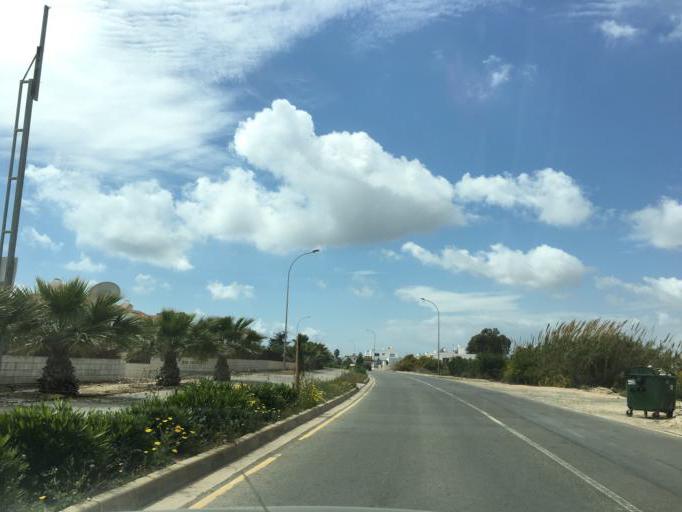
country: CY
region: Ammochostos
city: Liopetri
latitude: 34.9813
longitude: 33.9292
